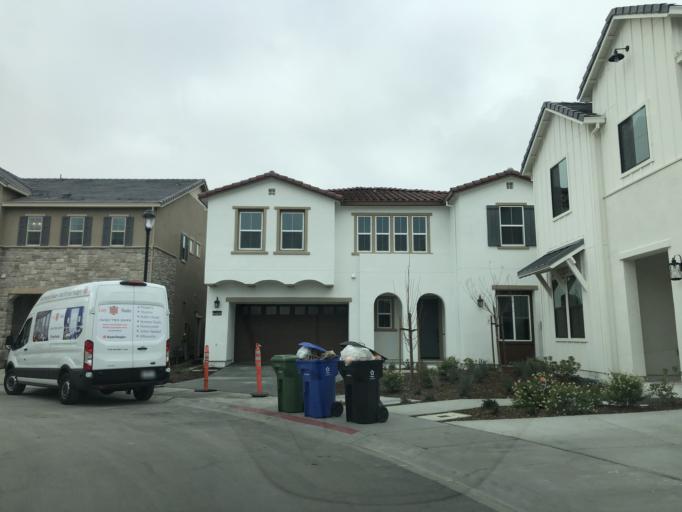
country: US
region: California
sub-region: Alameda County
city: Fremont
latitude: 37.5144
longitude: -122.0016
